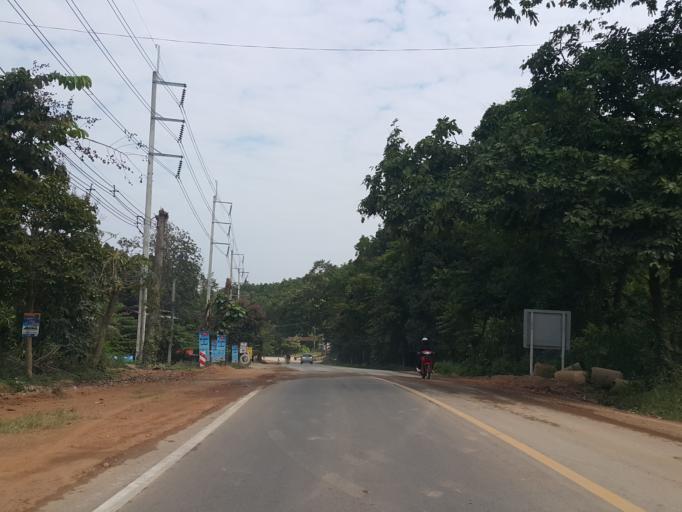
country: TH
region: Mae Hong Son
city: Mae Hong Son
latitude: 19.3158
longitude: 97.9657
